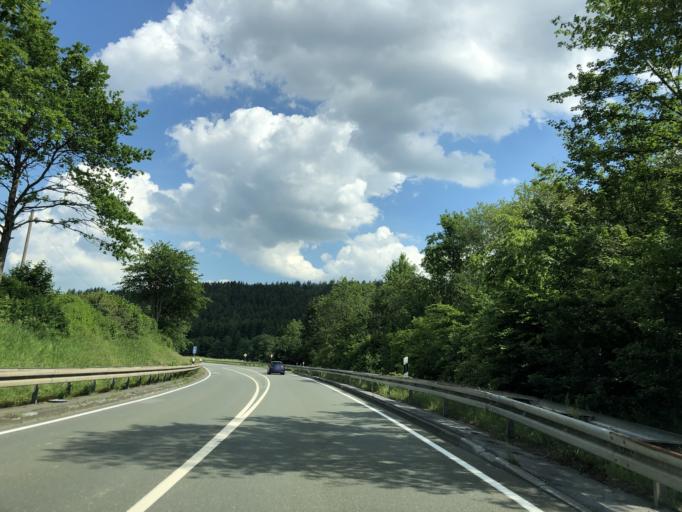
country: DE
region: North Rhine-Westphalia
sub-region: Regierungsbezirk Arnsberg
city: Ruthen
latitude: 51.4328
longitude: 8.4486
